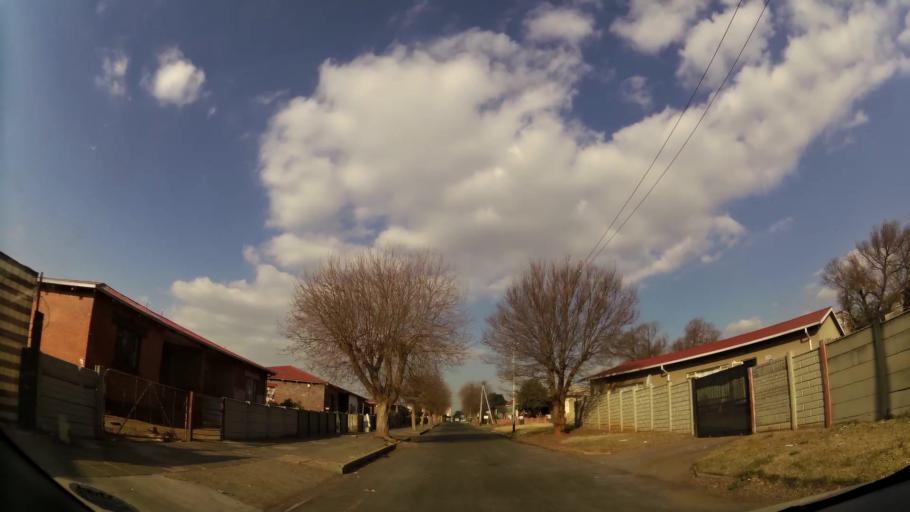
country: ZA
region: Gauteng
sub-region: West Rand District Municipality
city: Krugersdorp
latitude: -26.0967
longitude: 27.7556
